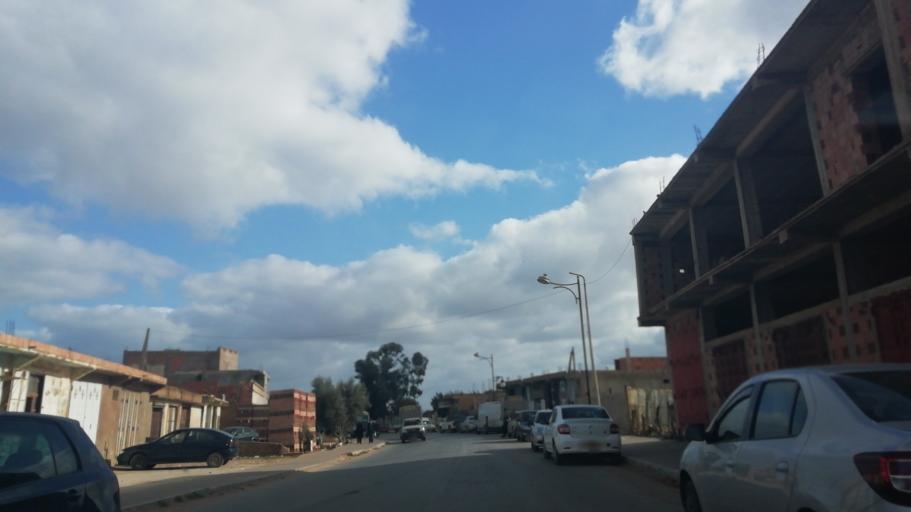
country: DZ
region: Relizane
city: Mazouna
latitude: 36.2702
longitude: 0.6315
